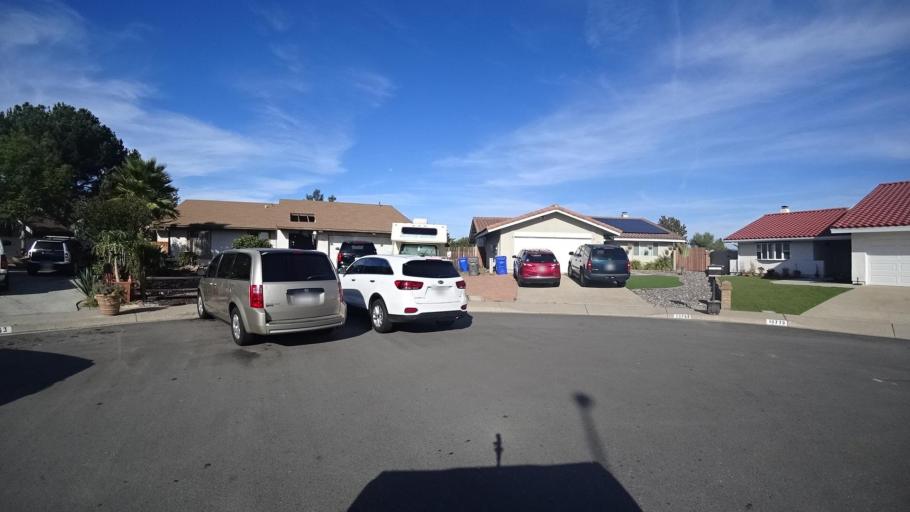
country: US
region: California
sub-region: San Diego County
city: Casa de Oro-Mount Helix
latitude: 32.7408
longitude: -116.9615
